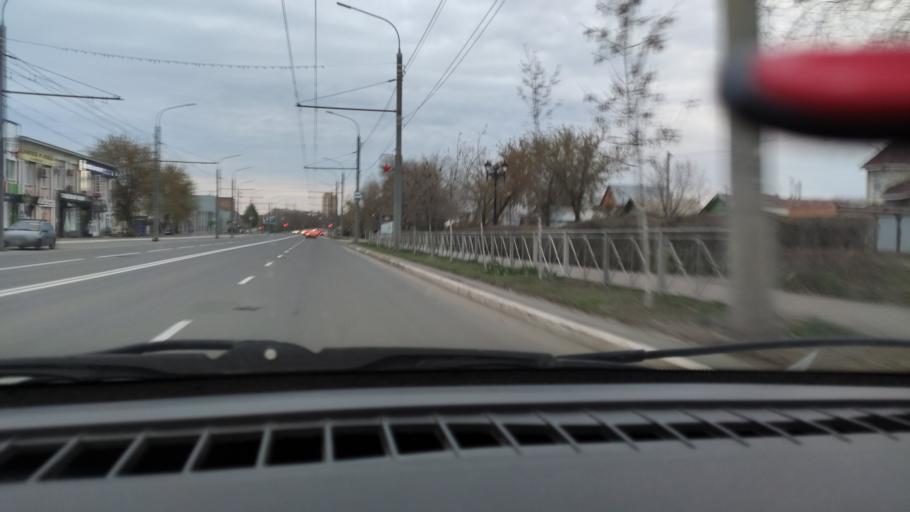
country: RU
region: Orenburg
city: Orenburg
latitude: 51.7836
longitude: 55.1165
